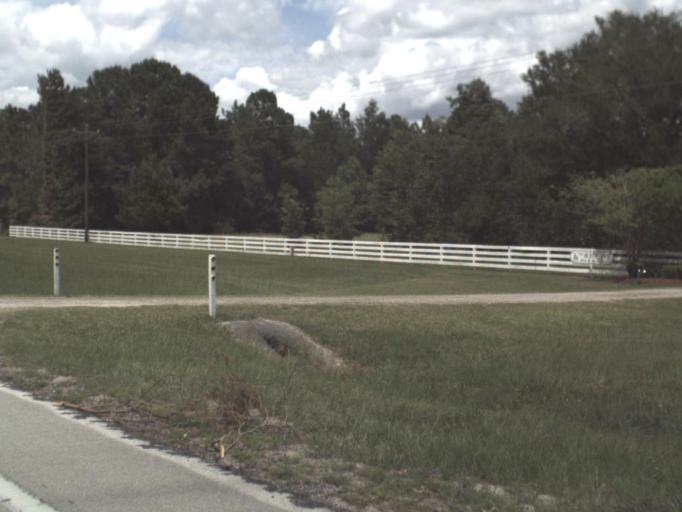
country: US
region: Florida
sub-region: Alachua County
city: High Springs
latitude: 29.7974
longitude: -82.6083
